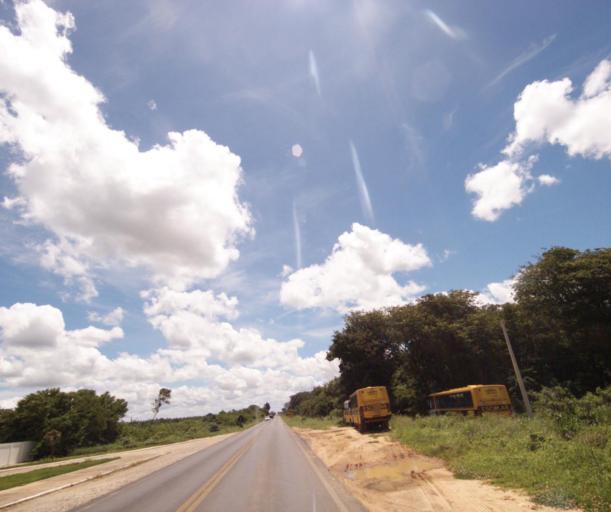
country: BR
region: Bahia
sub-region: Bom Jesus Da Lapa
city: Bom Jesus da Lapa
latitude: -13.2630
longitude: -43.5468
